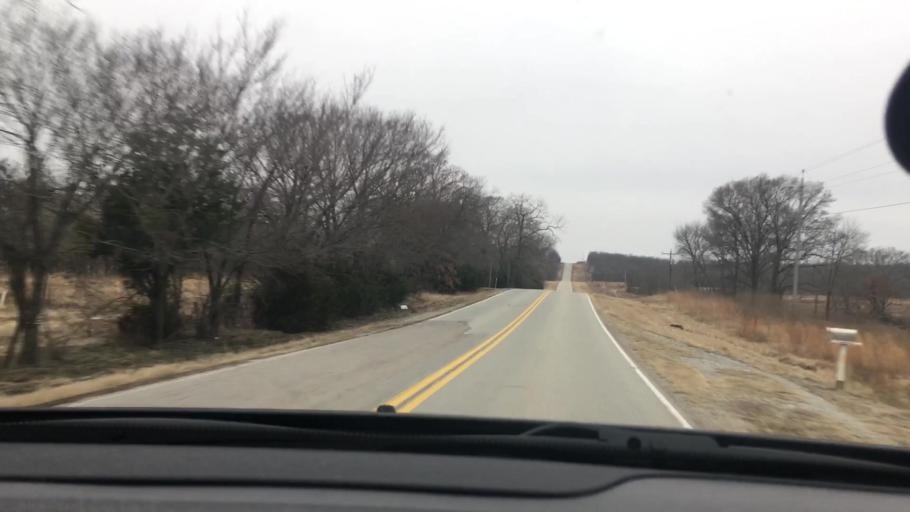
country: US
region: Oklahoma
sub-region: Coal County
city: Coalgate
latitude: 34.5057
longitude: -96.3080
